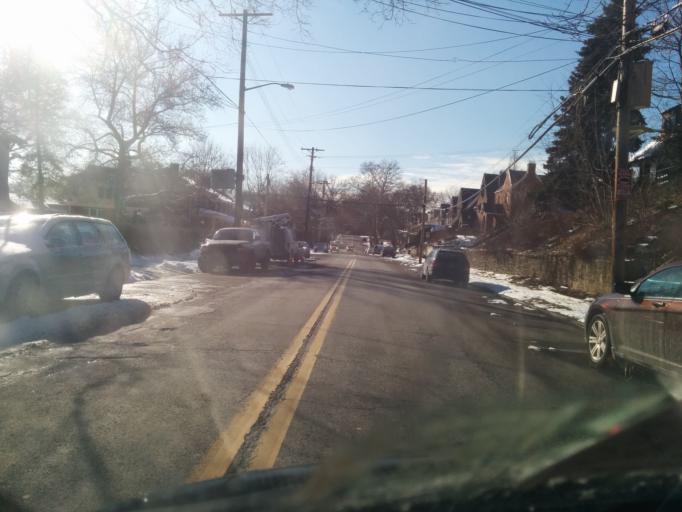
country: US
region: Pennsylvania
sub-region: Allegheny County
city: Homestead
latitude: 40.4323
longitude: -79.9297
